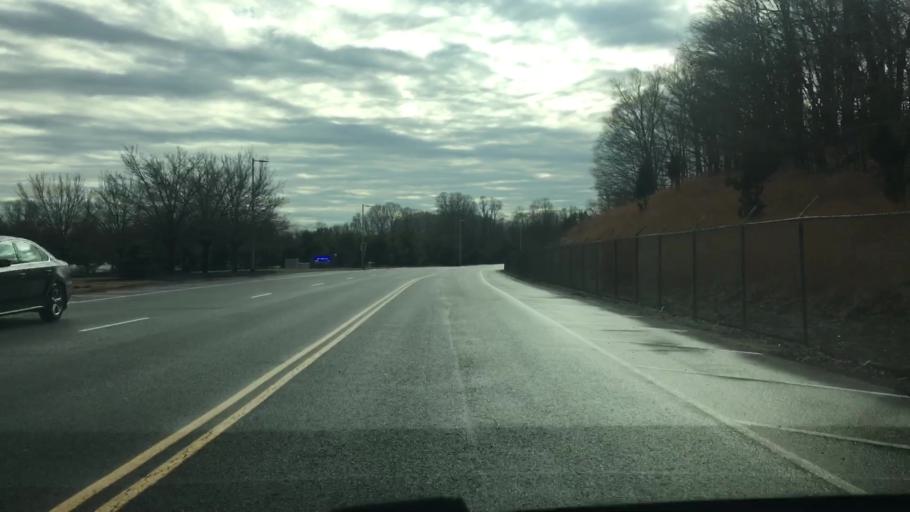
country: US
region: Connecticut
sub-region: Middlesex County
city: Higganum
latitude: 41.5355
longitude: -72.5616
